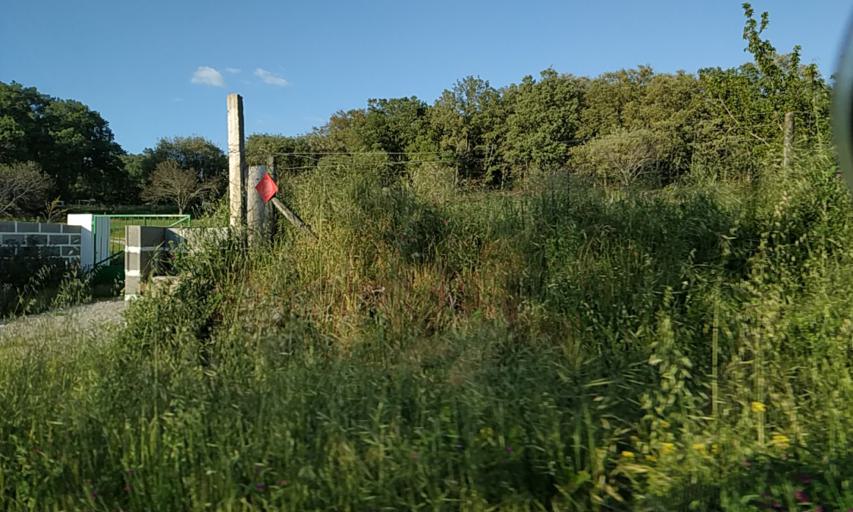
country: PT
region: Portalegre
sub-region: Marvao
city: Marvao
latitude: 39.3522
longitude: -7.4058
